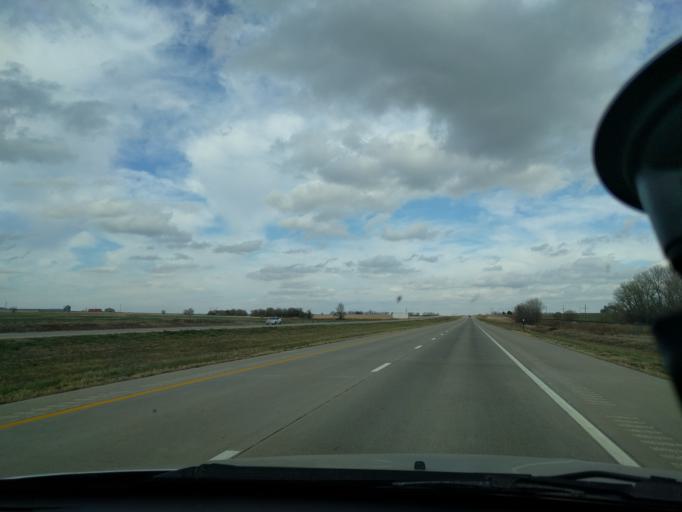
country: US
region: Kansas
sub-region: Reno County
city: Buhler
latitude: 38.1693
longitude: -97.8277
